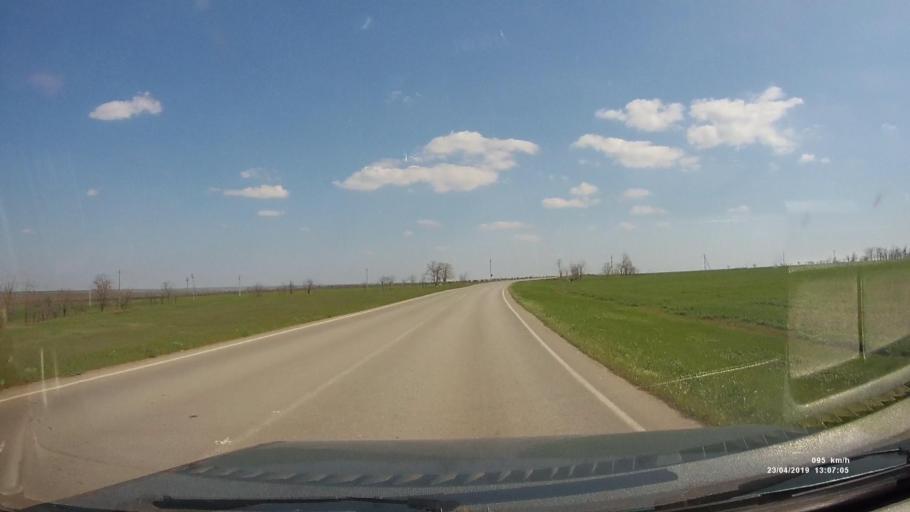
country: RU
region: Kalmykiya
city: Yashalta
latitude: 46.5916
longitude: 42.7544
